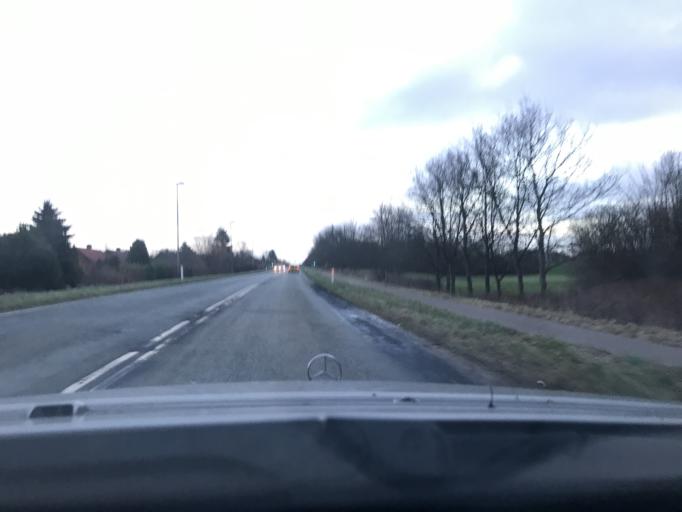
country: DK
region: South Denmark
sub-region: Sonderborg Kommune
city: Nordborg
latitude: 55.0508
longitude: 9.7727
